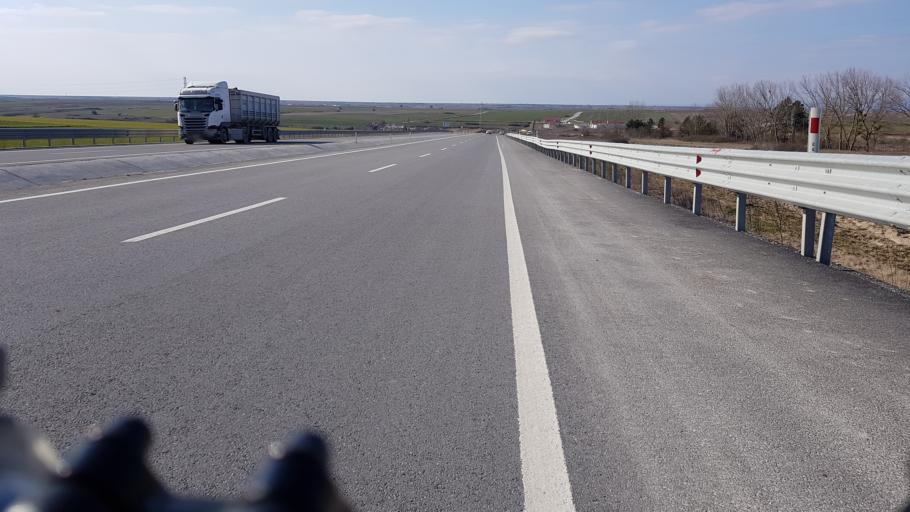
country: TR
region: Tekirdag
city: Saray
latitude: 41.4203
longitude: 27.9190
